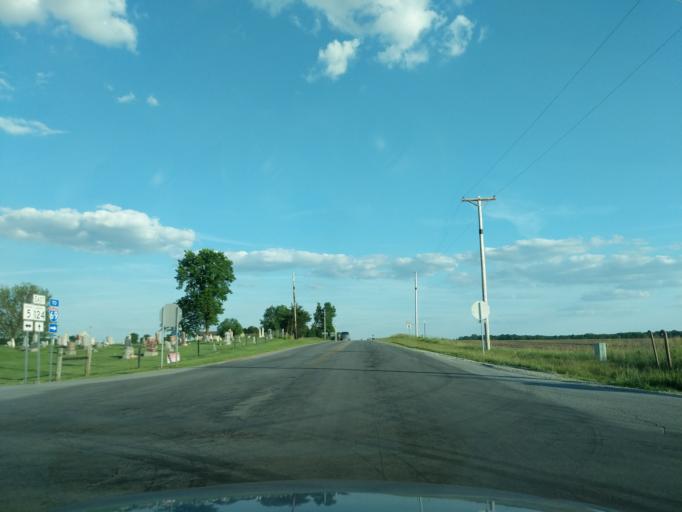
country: US
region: Indiana
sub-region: Huntington County
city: Warren
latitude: 40.7420
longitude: -85.4445
